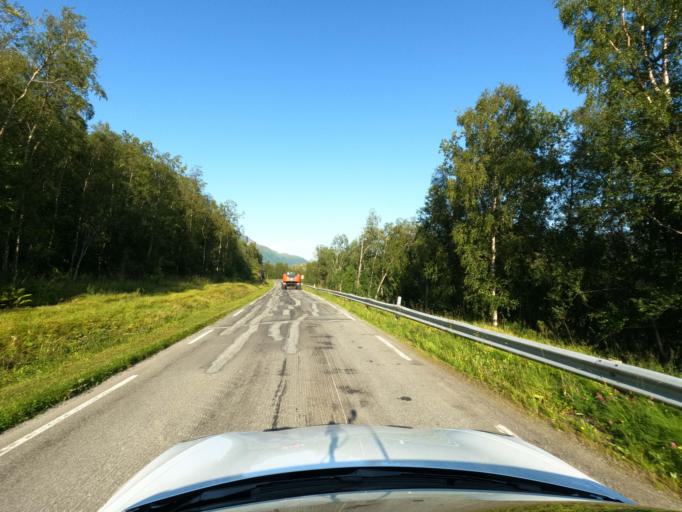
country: NO
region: Nordland
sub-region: Narvik
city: Bjerkvik
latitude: 68.5528
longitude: 17.5893
